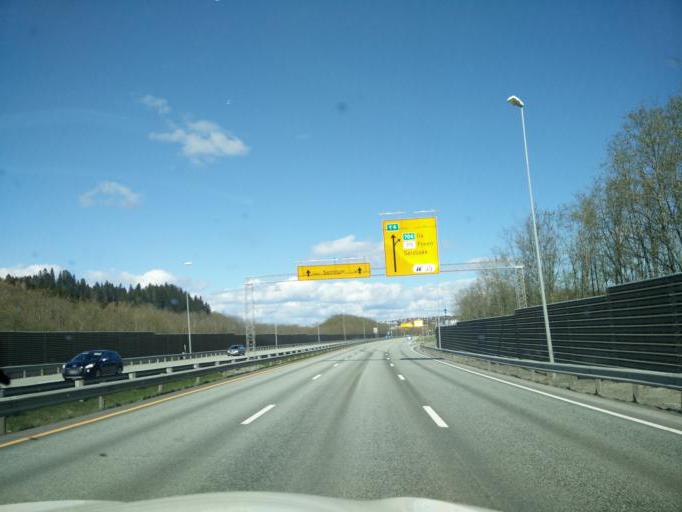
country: NO
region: Sor-Trondelag
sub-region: Trondheim
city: Trondheim
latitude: 63.3890
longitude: 10.3807
